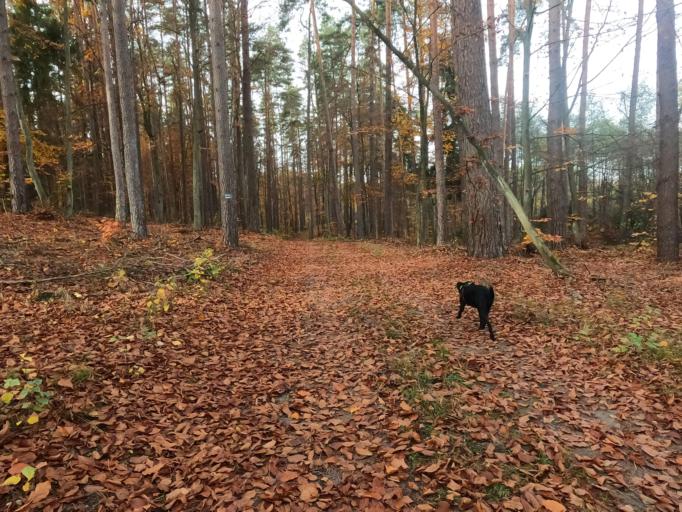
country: PL
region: Pomeranian Voivodeship
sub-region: Powiat starogardzki
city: Skarszewy
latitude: 54.0106
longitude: 18.4641
